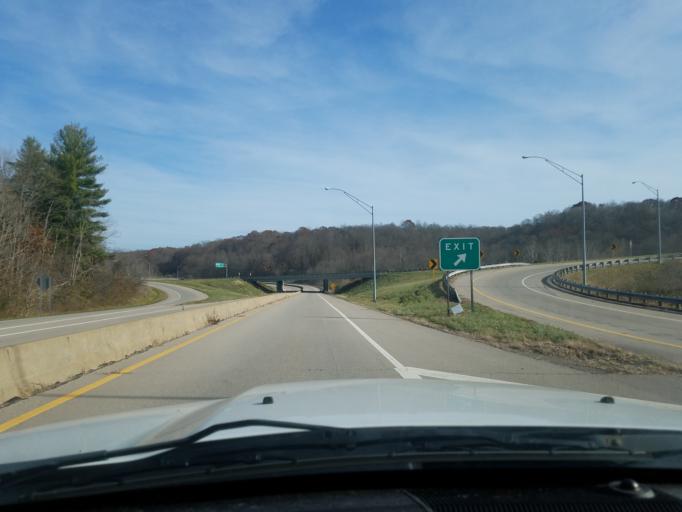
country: US
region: West Virginia
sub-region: Wood County
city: Washington
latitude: 39.2122
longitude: -81.8170
